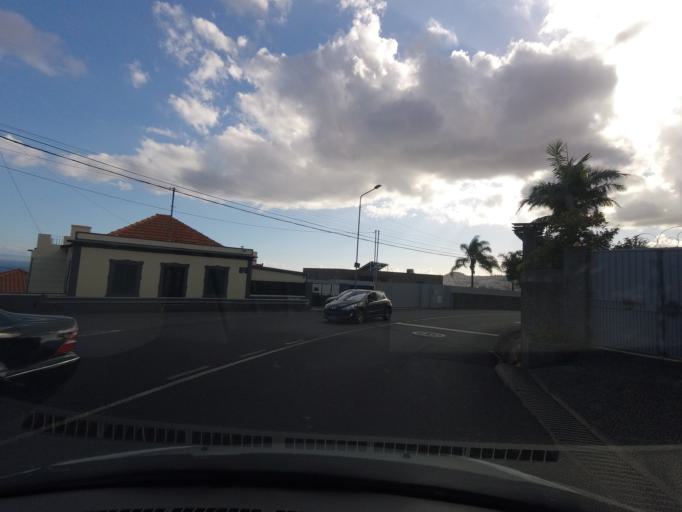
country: PT
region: Madeira
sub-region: Funchal
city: Nossa Senhora do Monte
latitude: 32.6579
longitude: -16.8968
